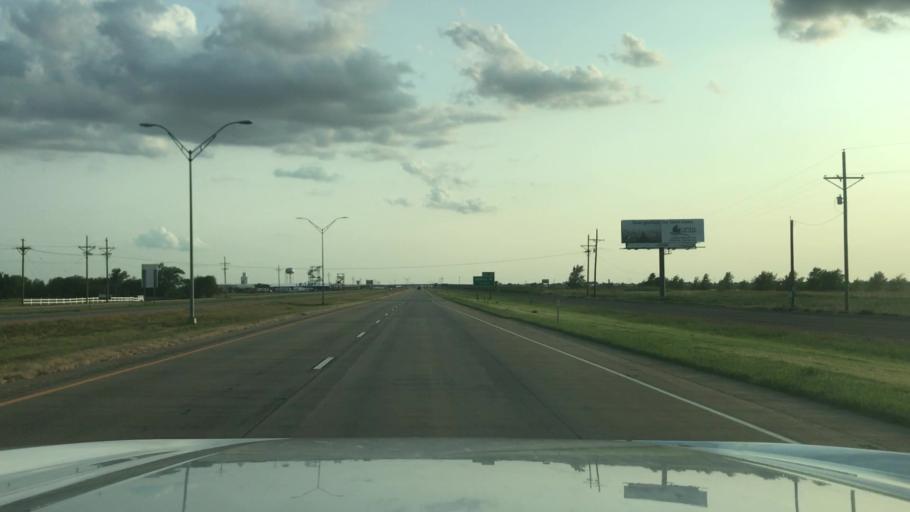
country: US
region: Texas
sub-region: Hale County
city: Seth Ward
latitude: 34.2284
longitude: -101.7150
